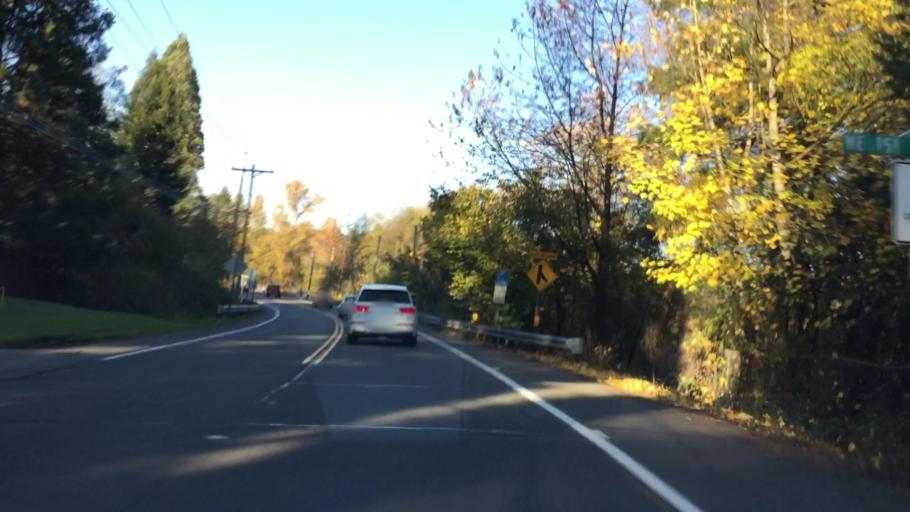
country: US
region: Washington
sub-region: King County
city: Cottage Lake
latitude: 47.7372
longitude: -122.0802
